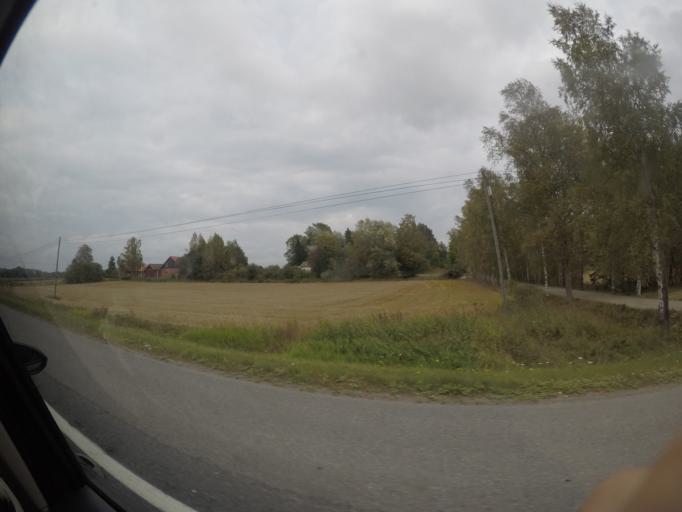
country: FI
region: Haeme
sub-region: Haemeenlinna
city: Haemeenlinna
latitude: 61.0281
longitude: 24.4201
